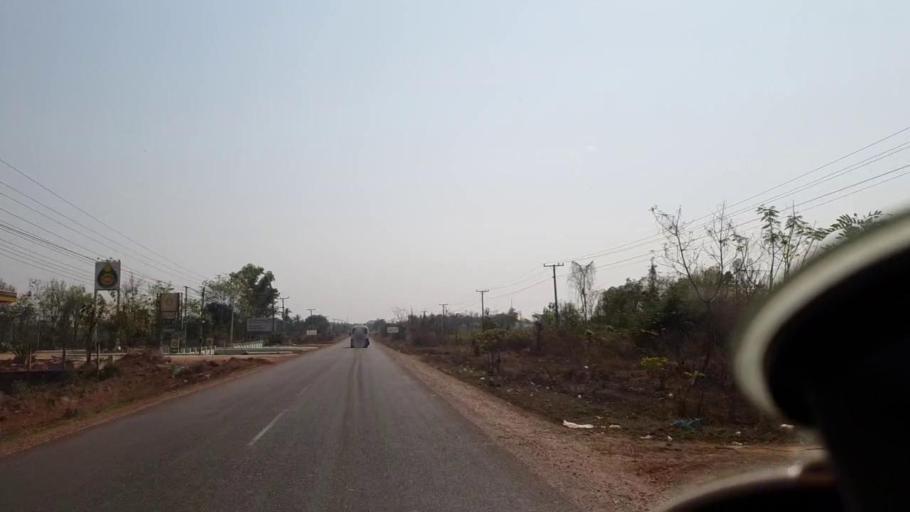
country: TH
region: Nong Khai
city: Nong Khai
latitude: 18.0556
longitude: 102.8294
